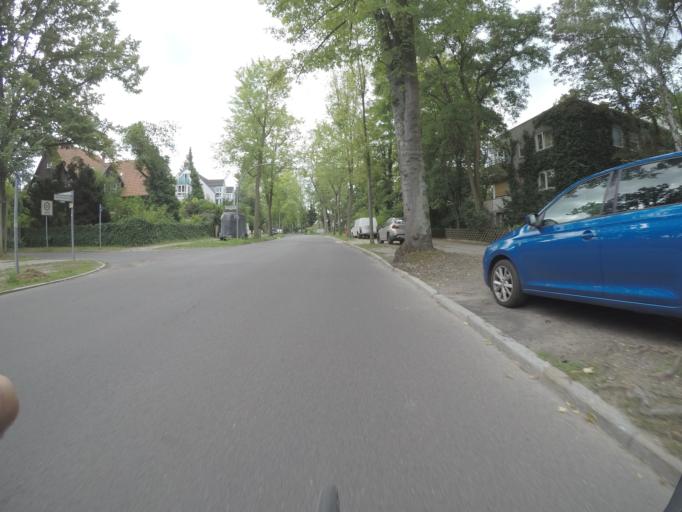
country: DE
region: Berlin
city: Frohnau
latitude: 52.6335
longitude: 13.2730
